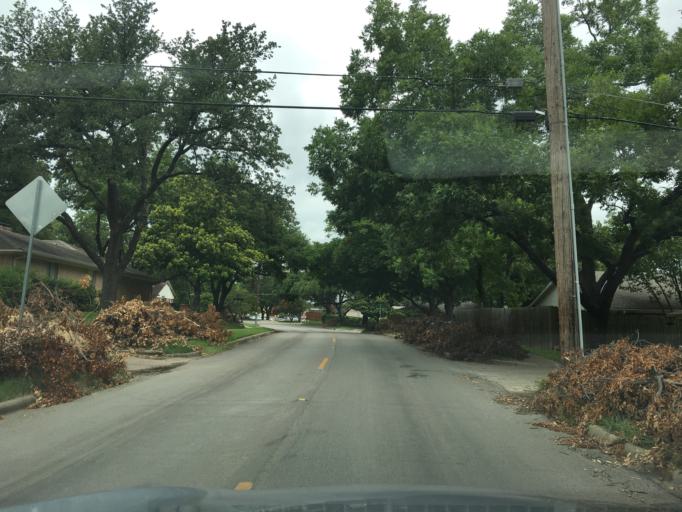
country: US
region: Texas
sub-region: Dallas County
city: Highland Park
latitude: 32.8617
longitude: -96.7420
